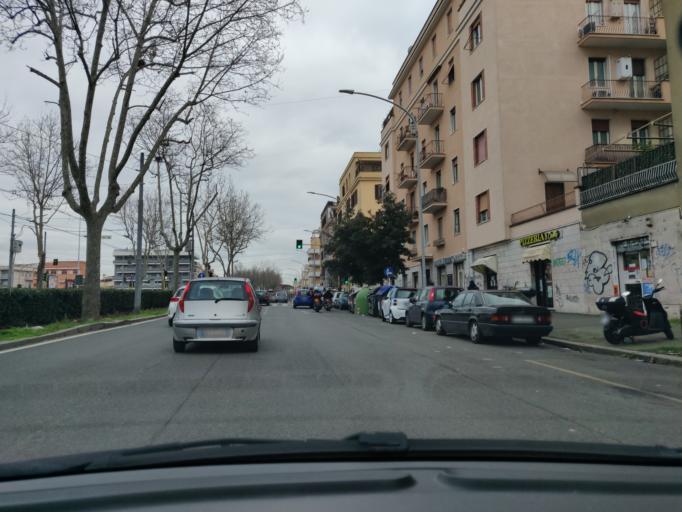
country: VA
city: Vatican City
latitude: 41.8752
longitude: 12.4456
